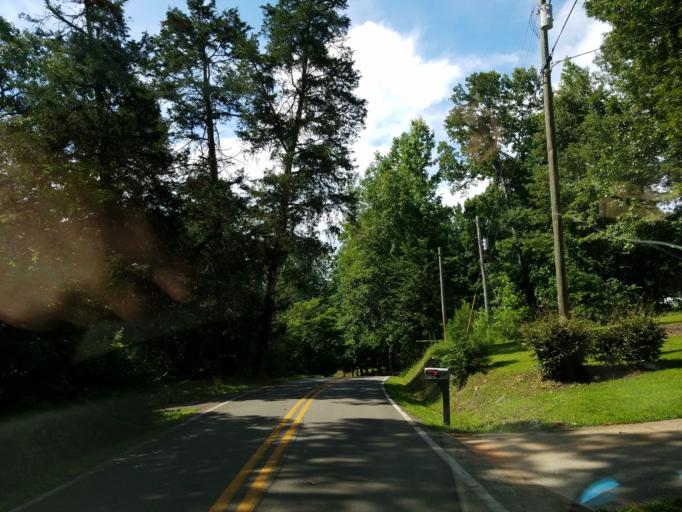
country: US
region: Georgia
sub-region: Pickens County
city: Nelson
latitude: 34.3776
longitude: -84.3697
